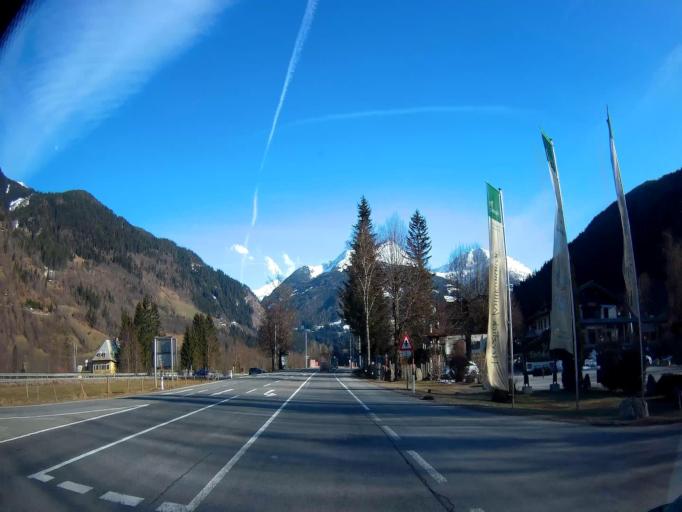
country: AT
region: Salzburg
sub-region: Politischer Bezirk Sankt Johann im Pongau
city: Bad Gastein
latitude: 47.1435
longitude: 13.1210
